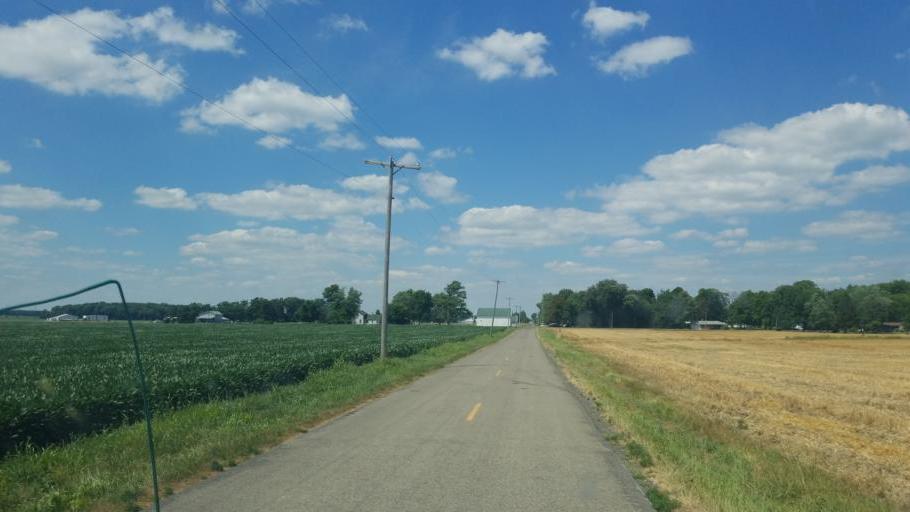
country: US
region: Ohio
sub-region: Defiance County
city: Hicksville
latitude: 41.3072
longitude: -84.7282
